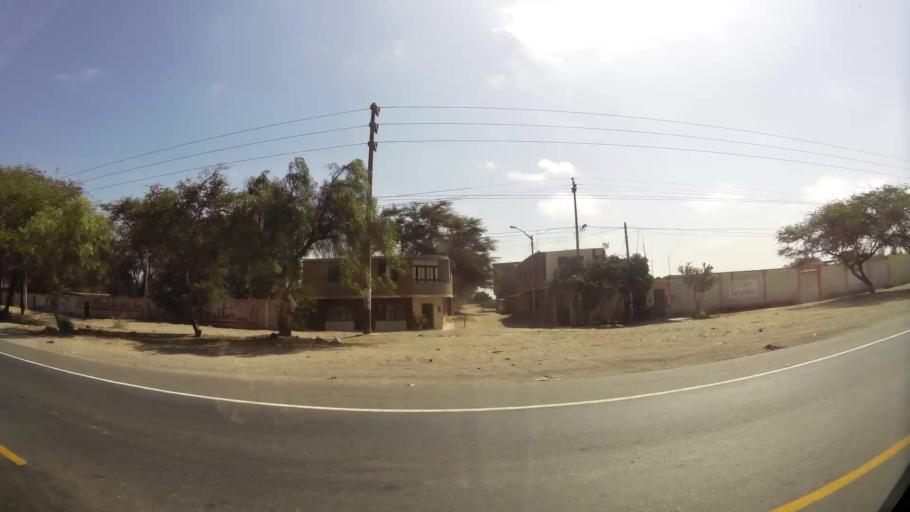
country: PE
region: Lambayeque
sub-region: Provincia de Chiclayo
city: Reque
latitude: -6.8237
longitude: -79.8295
